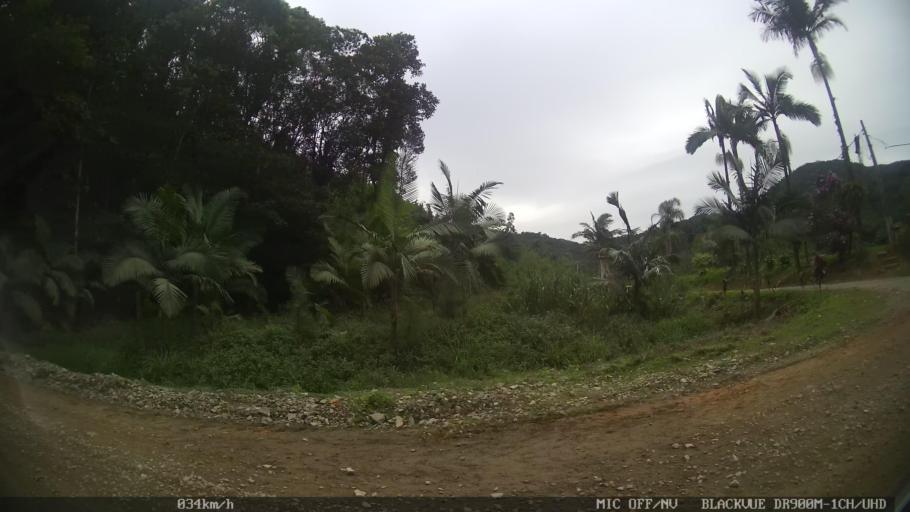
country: BR
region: Santa Catarina
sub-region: Joinville
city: Joinville
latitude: -26.2472
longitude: -48.9258
